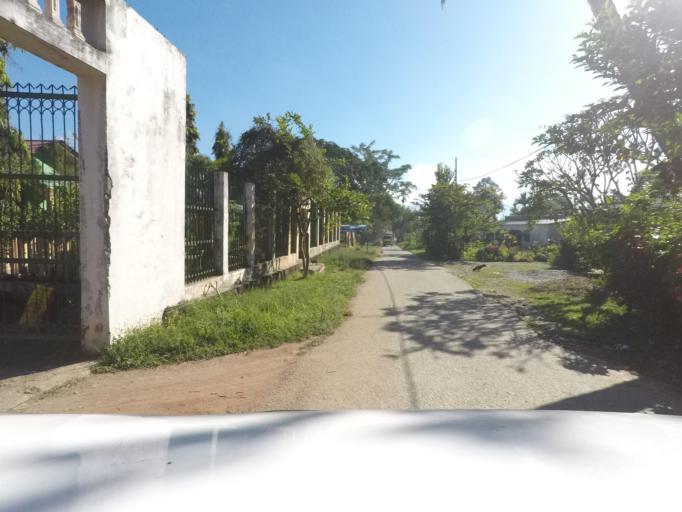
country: TL
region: Ermera
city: Gleno
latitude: -8.7309
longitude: 125.4325
